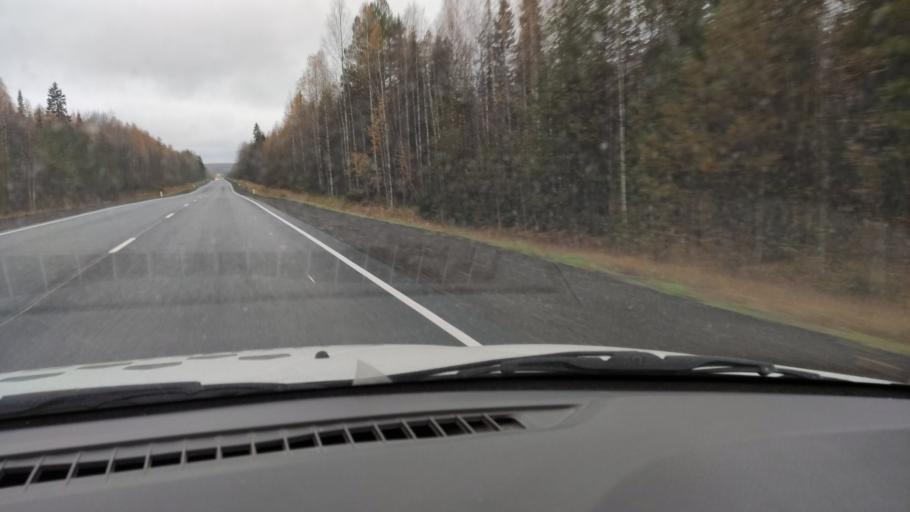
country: RU
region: Kirov
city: Chernaya Kholunitsa
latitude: 58.8860
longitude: 51.3947
